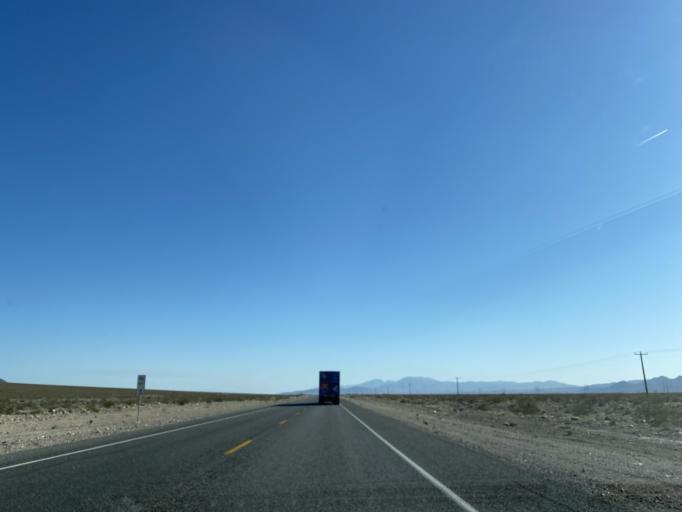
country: US
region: Nevada
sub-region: Nye County
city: Beatty
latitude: 36.8427
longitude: -116.7530
